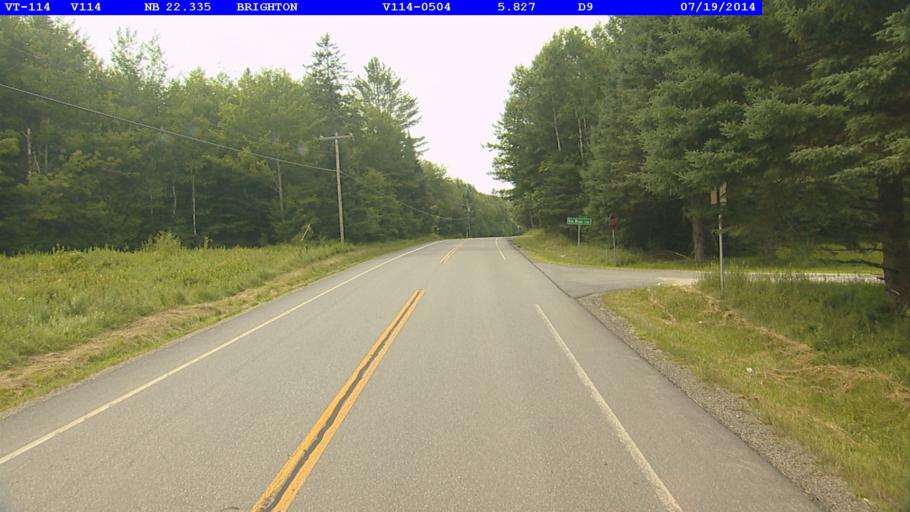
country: US
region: Vermont
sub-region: Caledonia County
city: Lyndonville
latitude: 44.8264
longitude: -71.9028
